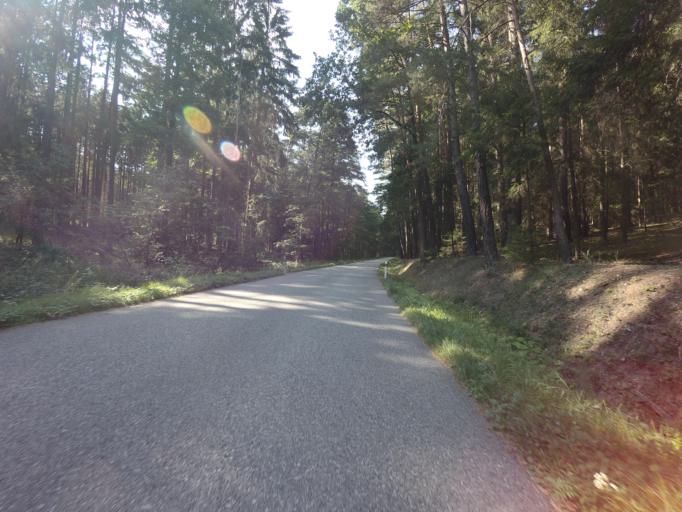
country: CZ
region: Jihocesky
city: Tyn nad Vltavou
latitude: 49.1567
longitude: 14.4320
